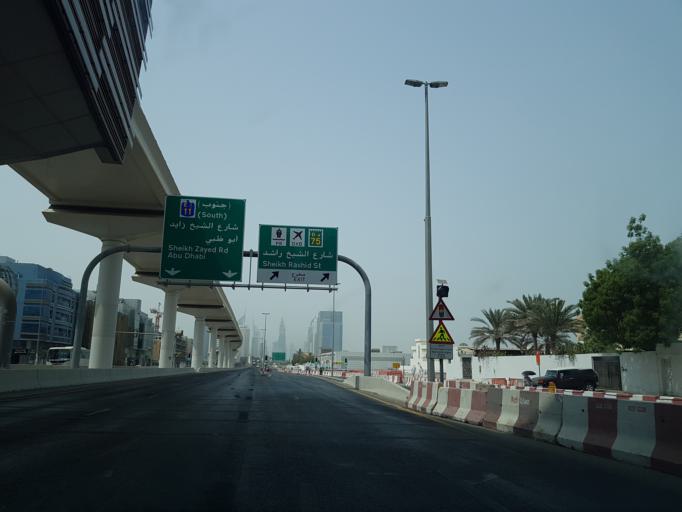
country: AE
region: Ash Shariqah
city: Sharjah
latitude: 25.2441
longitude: 55.2979
